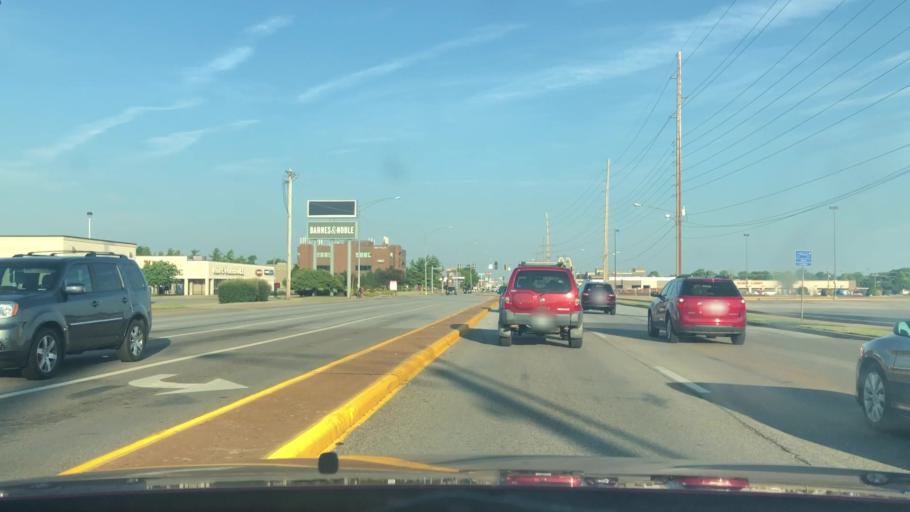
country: US
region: Missouri
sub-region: Greene County
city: Springfield
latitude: 37.1594
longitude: -93.2631
